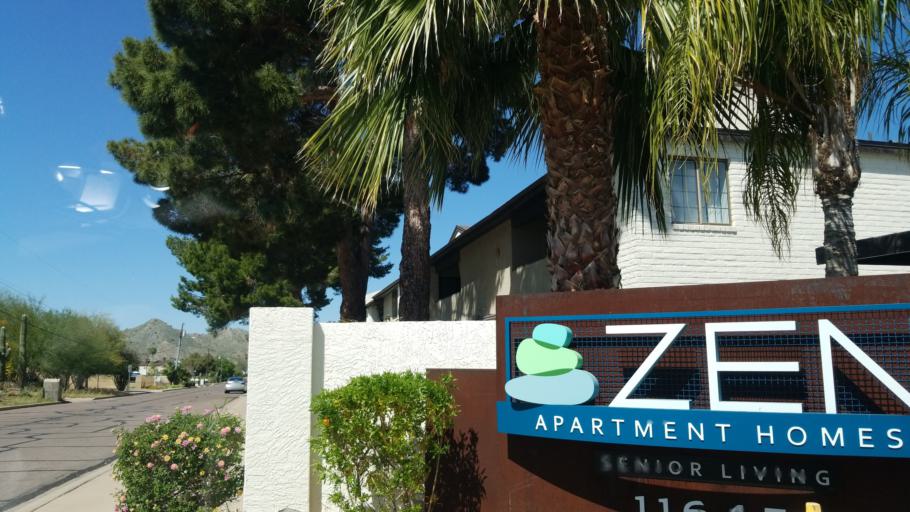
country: US
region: Arizona
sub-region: Maricopa County
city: Paradise Valley
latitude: 33.5927
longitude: -112.0272
